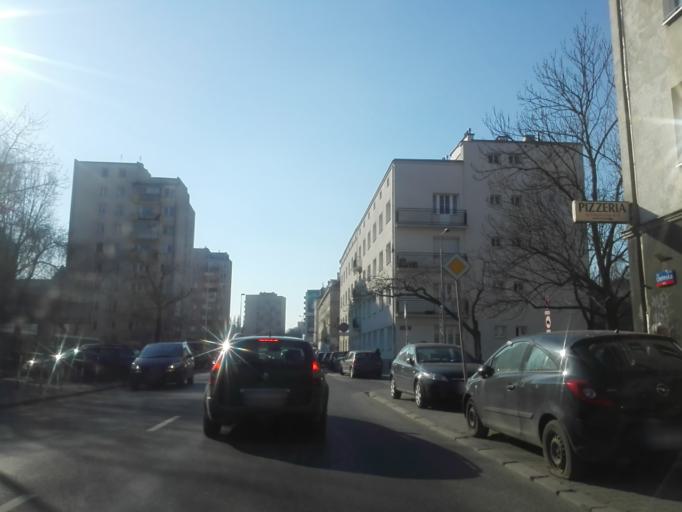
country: PL
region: Masovian Voivodeship
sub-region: Warszawa
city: Mokotow
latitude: 52.2021
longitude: 21.0384
